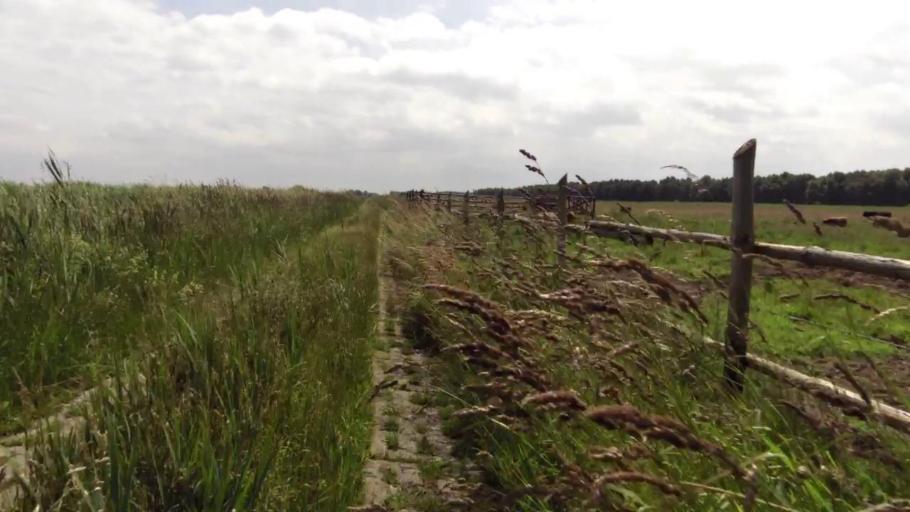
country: PL
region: West Pomeranian Voivodeship
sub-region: Powiat goleniowski
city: Stepnica
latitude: 53.7258
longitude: 14.6053
